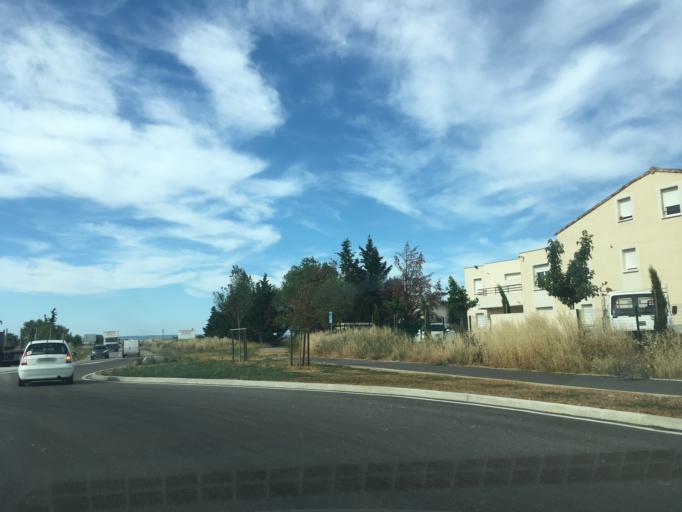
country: FR
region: Languedoc-Roussillon
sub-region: Departement du Gard
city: Garons
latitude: 43.7775
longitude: 4.4292
